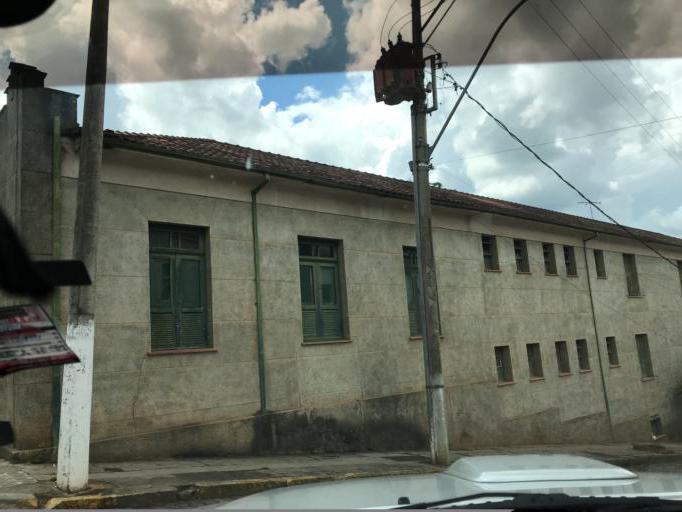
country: BR
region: Minas Gerais
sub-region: Cambuquira
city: Cambuquira
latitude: -21.8516
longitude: -45.2944
